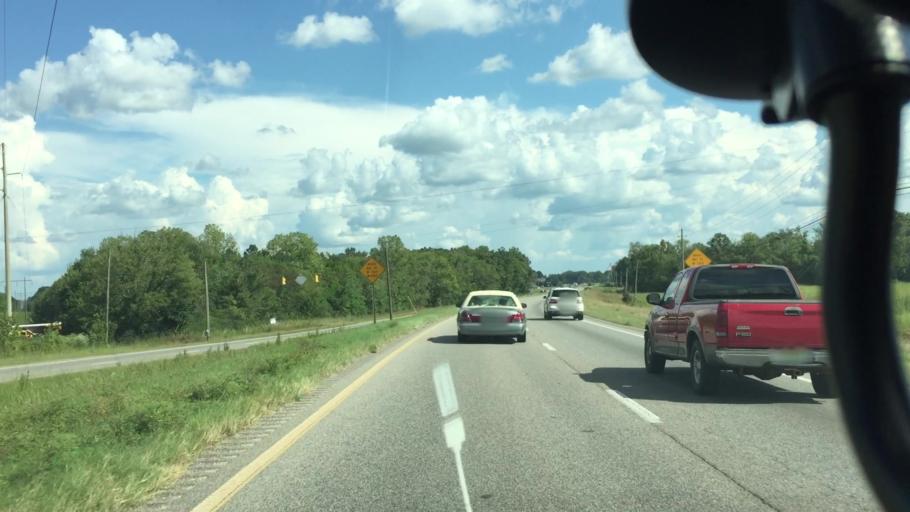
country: US
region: Alabama
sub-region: Montgomery County
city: Pike Road
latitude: 32.2947
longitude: -86.1934
